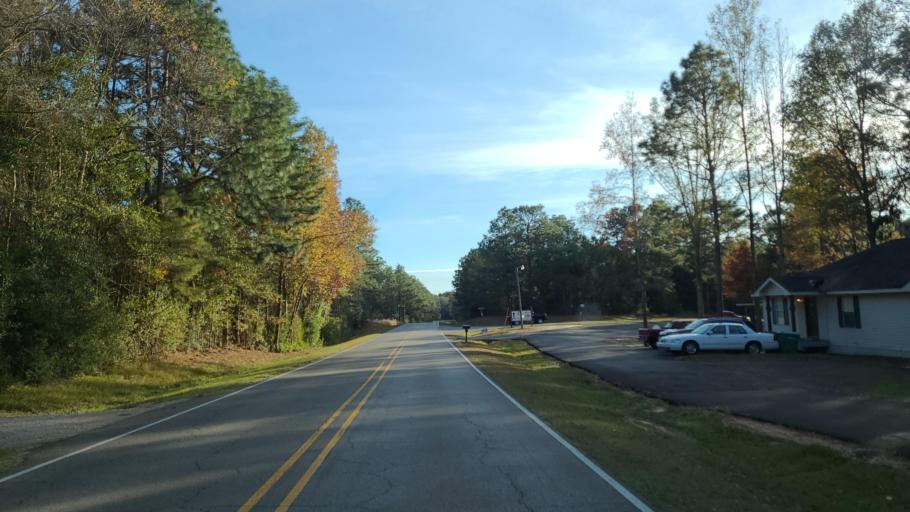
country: US
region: Mississippi
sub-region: Forrest County
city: Hattiesburg
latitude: 31.2267
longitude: -89.3042
